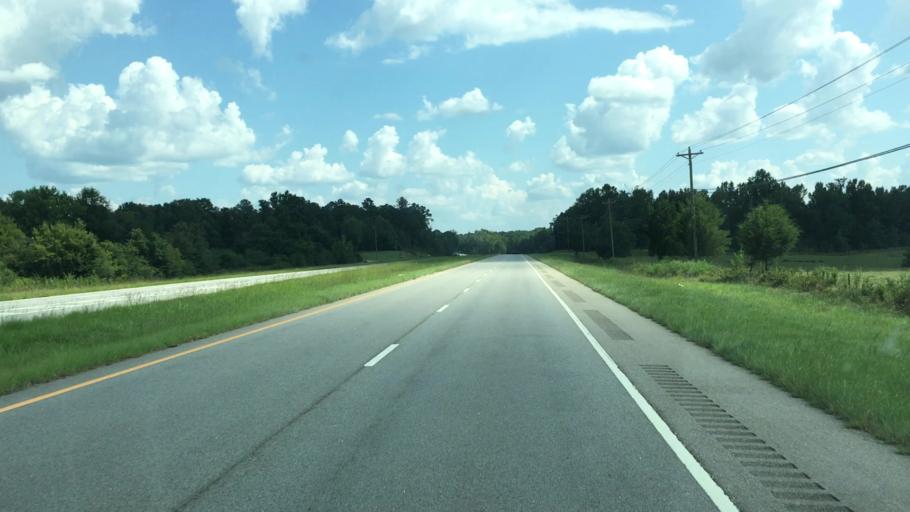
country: US
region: Georgia
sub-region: Putnam County
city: Eatonton
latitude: 33.2479
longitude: -83.3258
